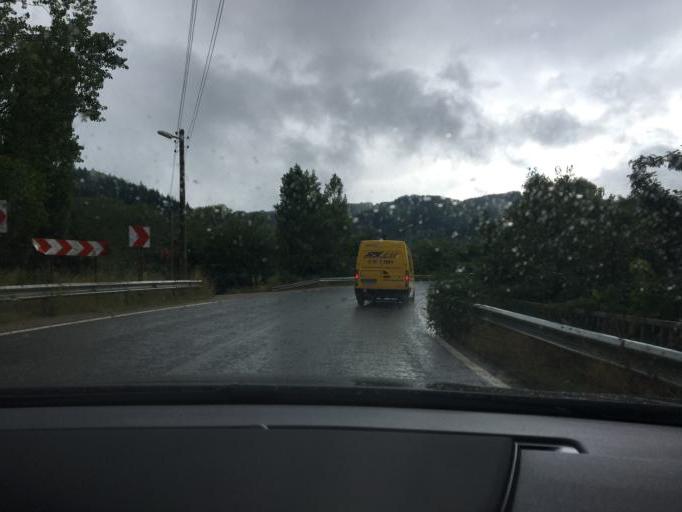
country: BG
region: Kyustendil
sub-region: Obshtina Kyustendil
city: Kyustendil
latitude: 42.2630
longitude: 22.5854
